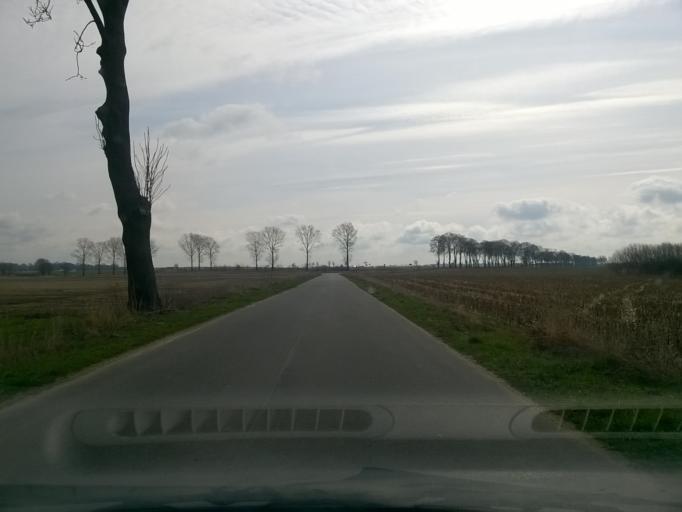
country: PL
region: Greater Poland Voivodeship
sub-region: Powiat wagrowiecki
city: Golancz
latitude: 52.9839
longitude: 17.3458
